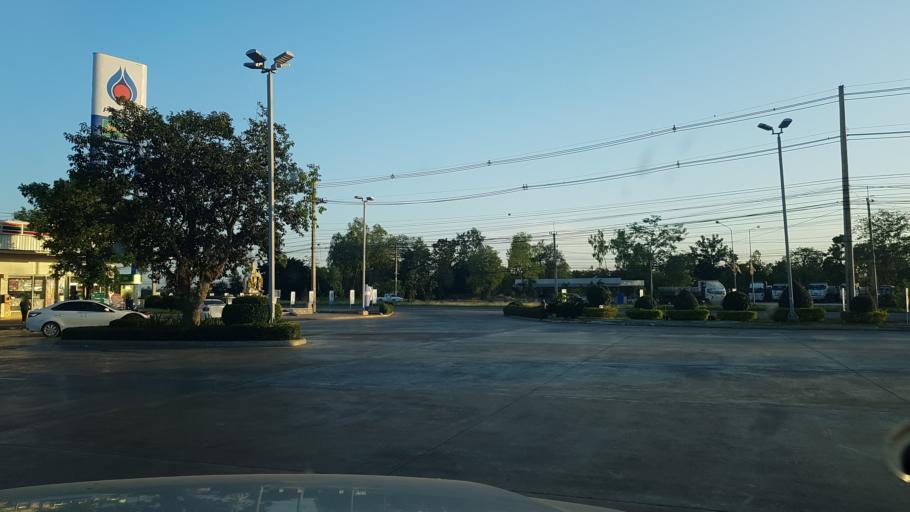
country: TH
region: Khon Kaen
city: Chum Phae
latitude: 16.5841
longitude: 102.0124
